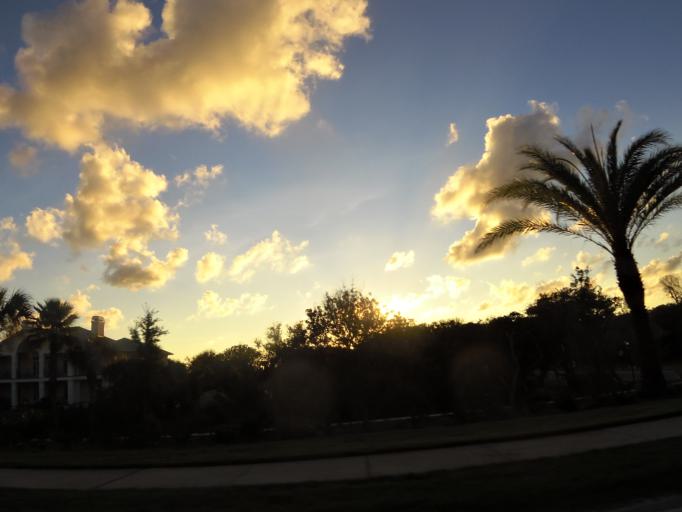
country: US
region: Florida
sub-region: Saint Johns County
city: Sawgrass
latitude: 30.1715
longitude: -81.3596
